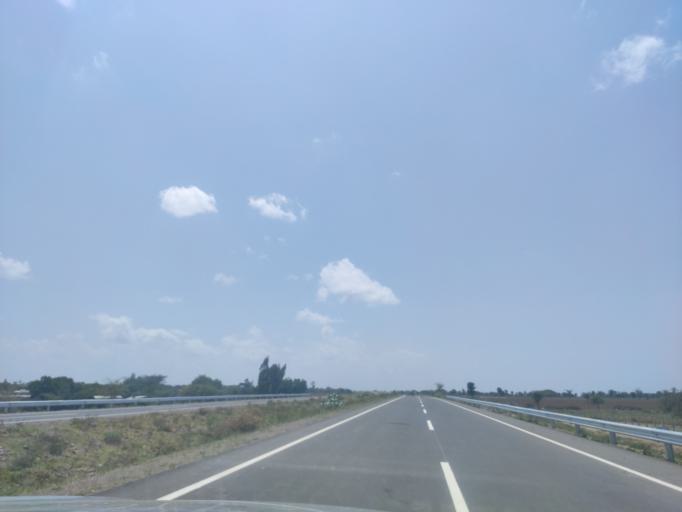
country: ET
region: Oromiya
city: Mojo
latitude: 8.3446
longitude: 38.9765
